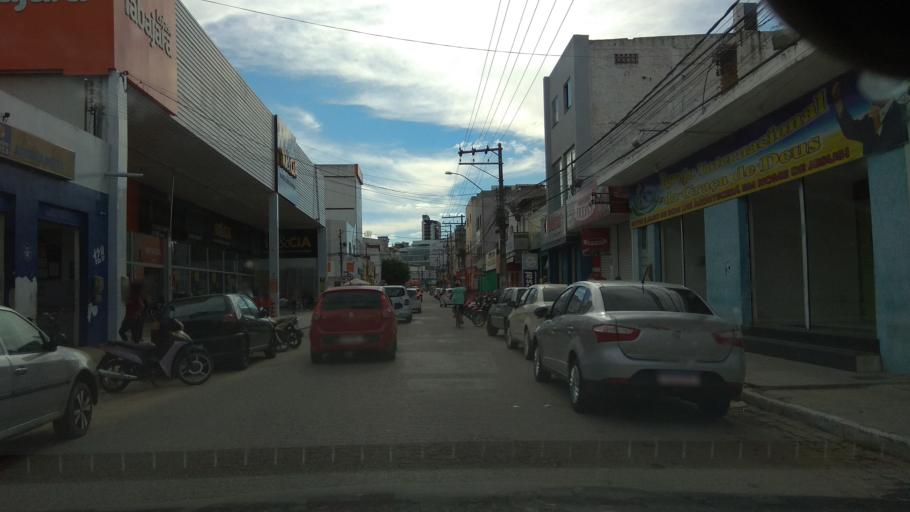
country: BR
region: Bahia
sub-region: Jequie
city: Jequie
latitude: -13.8607
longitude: -40.0778
